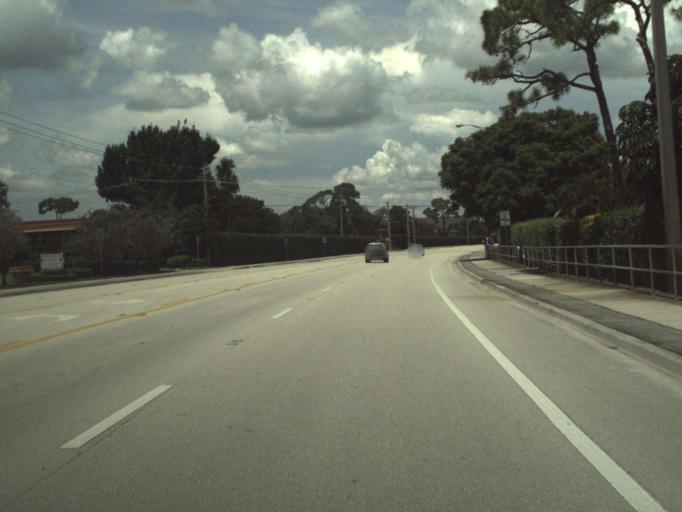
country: US
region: Florida
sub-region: Martin County
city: Sewall's Point
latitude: 27.1963
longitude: -80.2151
